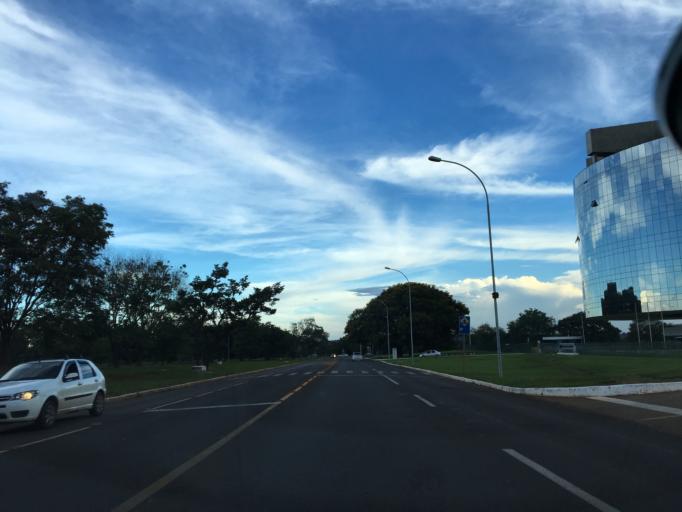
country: BR
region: Federal District
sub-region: Brasilia
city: Brasilia
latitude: -15.8062
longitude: -47.8594
